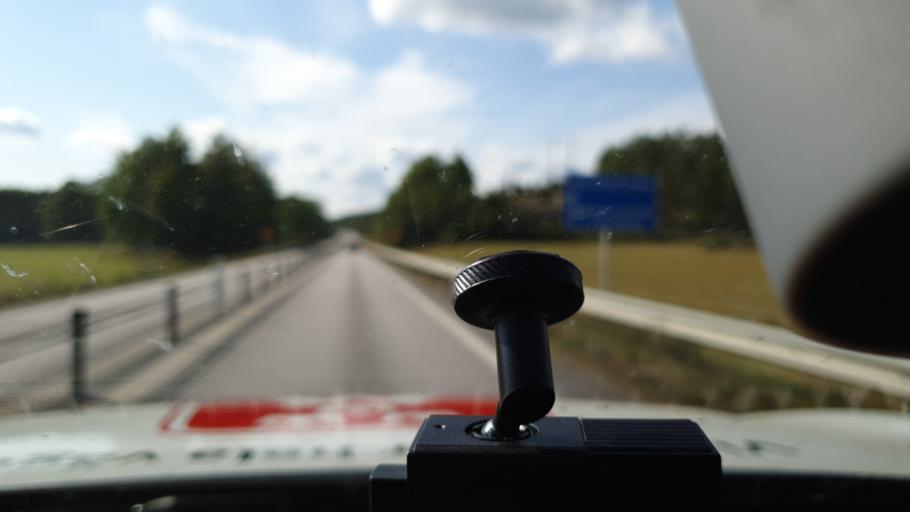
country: SE
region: Kalmar
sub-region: Vimmerby Kommun
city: Vimmerby
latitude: 57.7191
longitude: 16.0743
